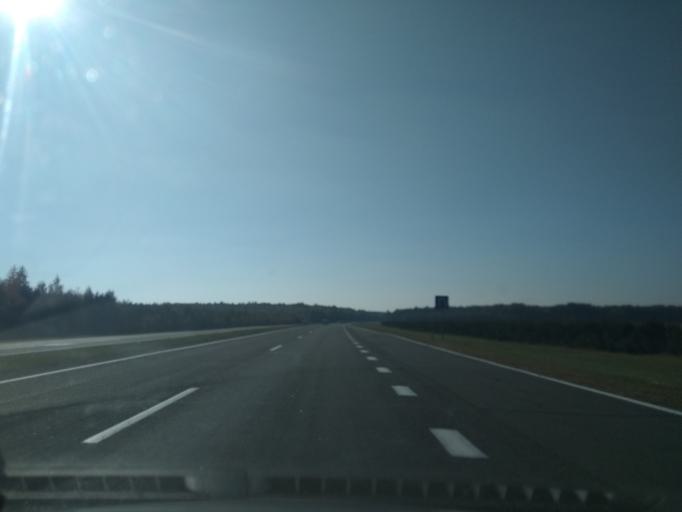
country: BY
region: Brest
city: Ivatsevichy
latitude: 52.7786
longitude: 25.5483
